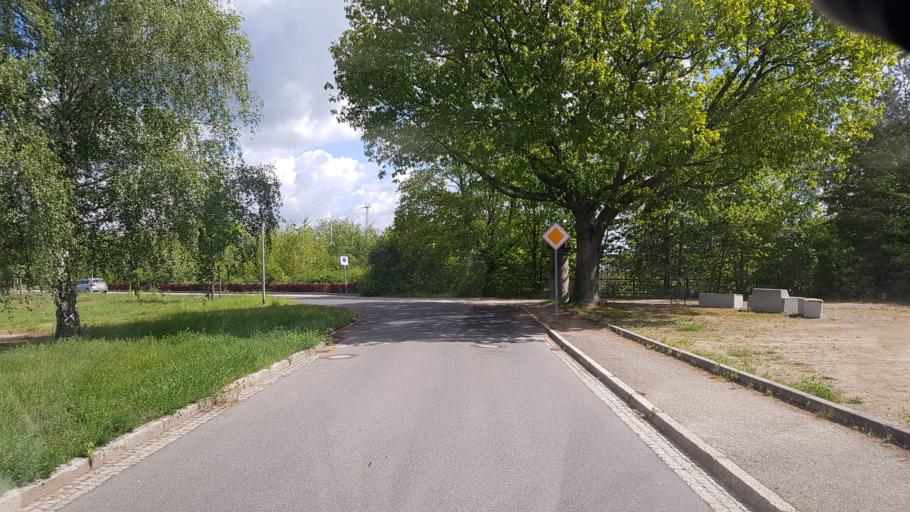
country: DE
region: Brandenburg
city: Grossraschen
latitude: 51.5891
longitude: 14.0144
